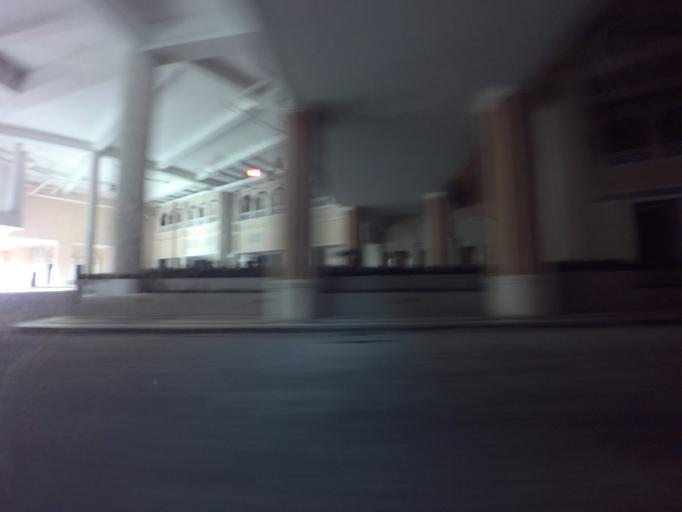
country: PH
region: Calabarzon
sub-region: Province of Rizal
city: Pateros
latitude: 14.5337
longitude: 121.0505
